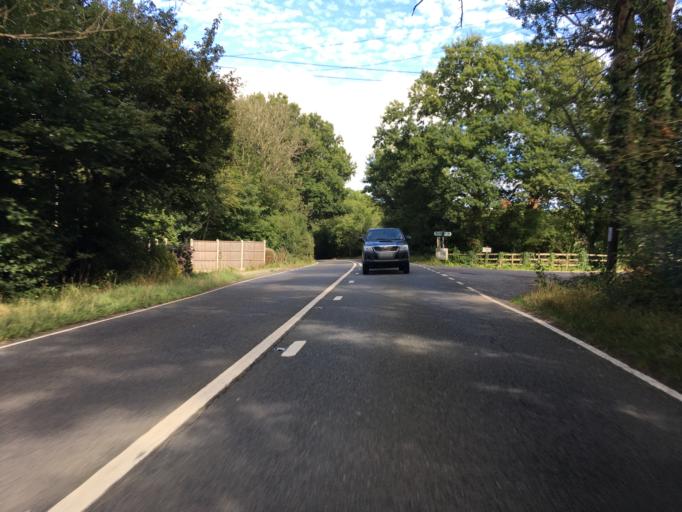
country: GB
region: England
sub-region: West Sussex
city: Billingshurst
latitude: 51.0525
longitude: -0.4073
